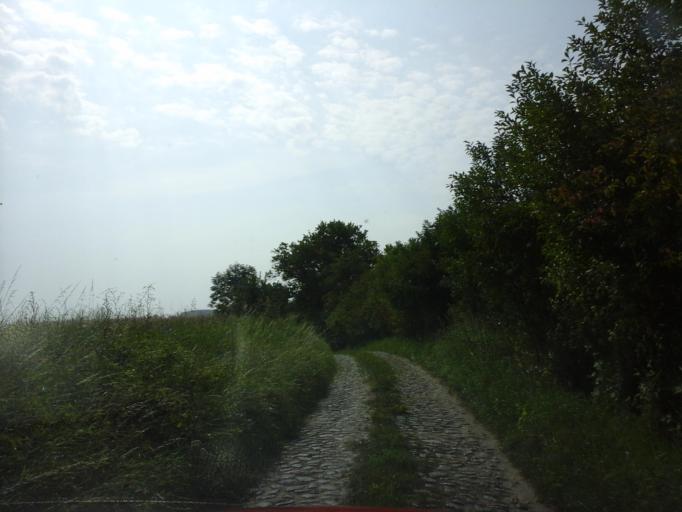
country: PL
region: West Pomeranian Voivodeship
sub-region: Powiat mysliborski
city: Barlinek
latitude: 53.0508
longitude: 15.1959
